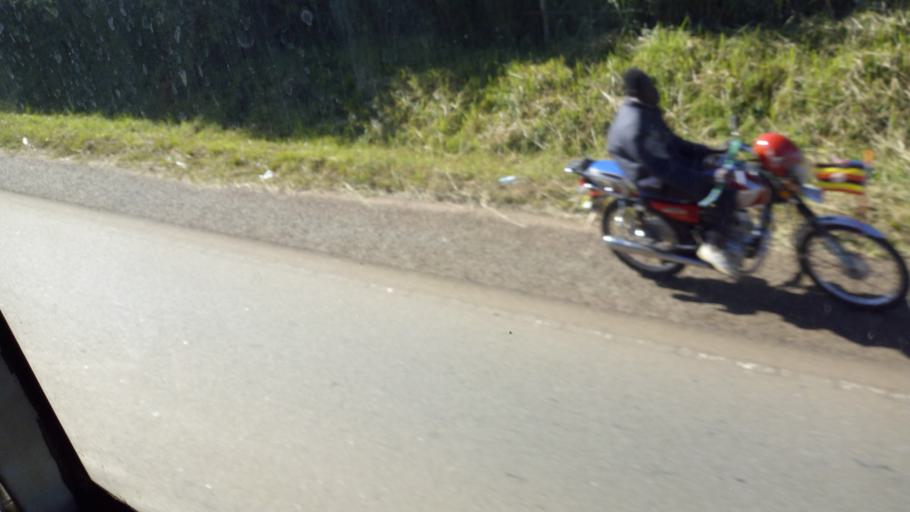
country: UG
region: Central Region
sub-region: Lyantonde District
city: Lyantonde
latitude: -0.4233
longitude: 31.1111
